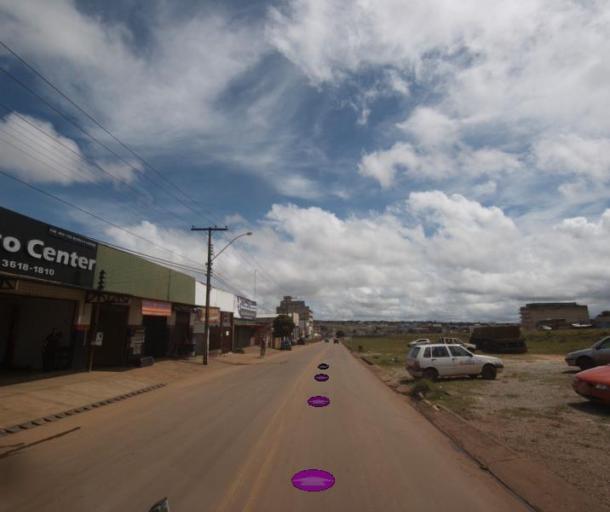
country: BR
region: Federal District
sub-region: Brasilia
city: Brasilia
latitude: -15.7460
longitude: -48.2666
